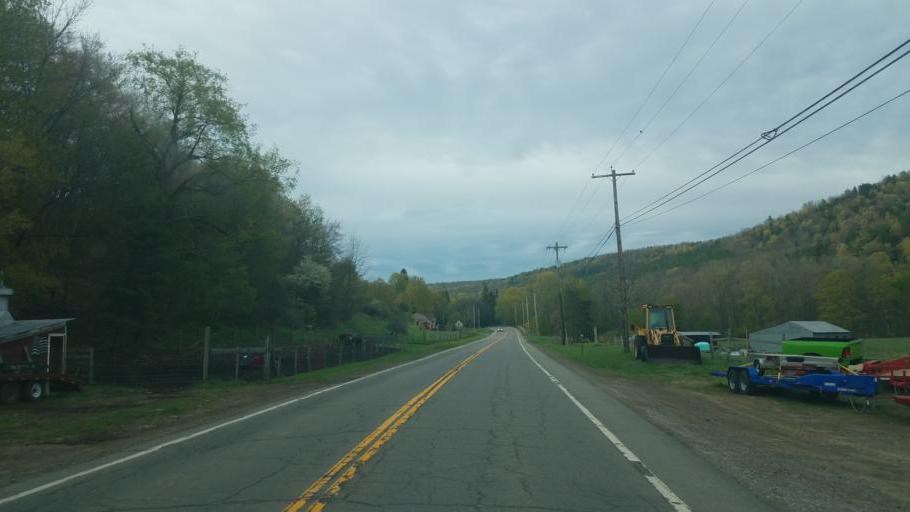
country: US
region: New York
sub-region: Steuben County
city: Canisteo
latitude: 42.2210
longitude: -77.5720
